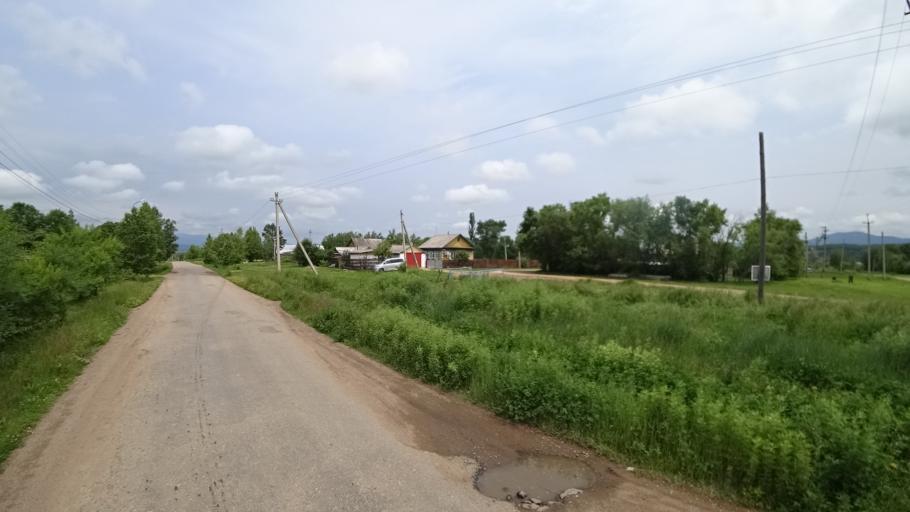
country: RU
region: Primorskiy
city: Novosysoyevka
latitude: 44.2325
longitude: 133.3600
